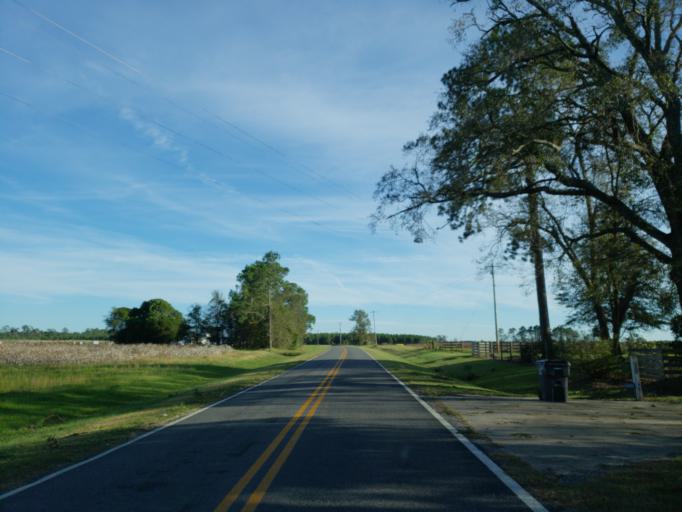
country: US
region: Georgia
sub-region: Dooly County
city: Vienna
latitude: 32.0516
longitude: -83.7608
